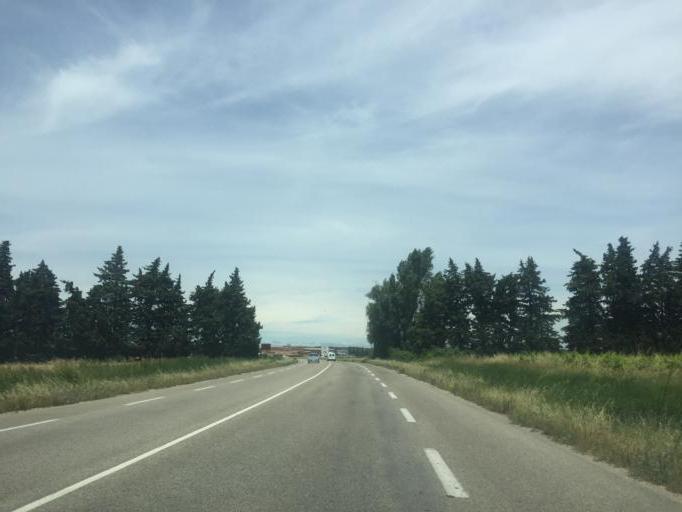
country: FR
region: Languedoc-Roussillon
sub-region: Departement du Gard
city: Les Angles
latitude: 43.9837
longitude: 4.7492
